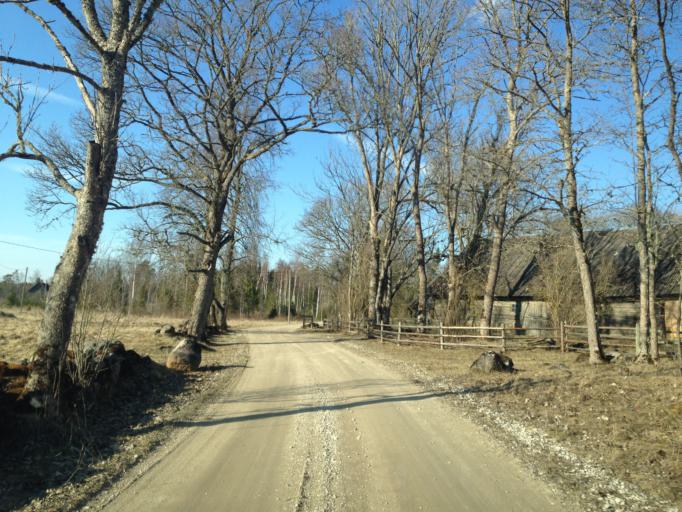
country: EE
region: Harju
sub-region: Nissi vald
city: Turba
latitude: 59.1225
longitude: 24.1632
